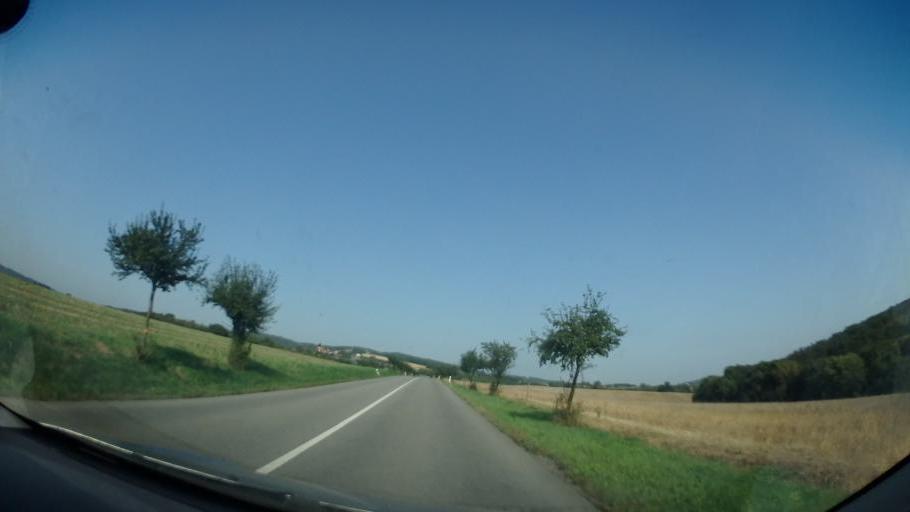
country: CZ
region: South Moravian
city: Kurim
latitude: 49.2472
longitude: 16.5287
